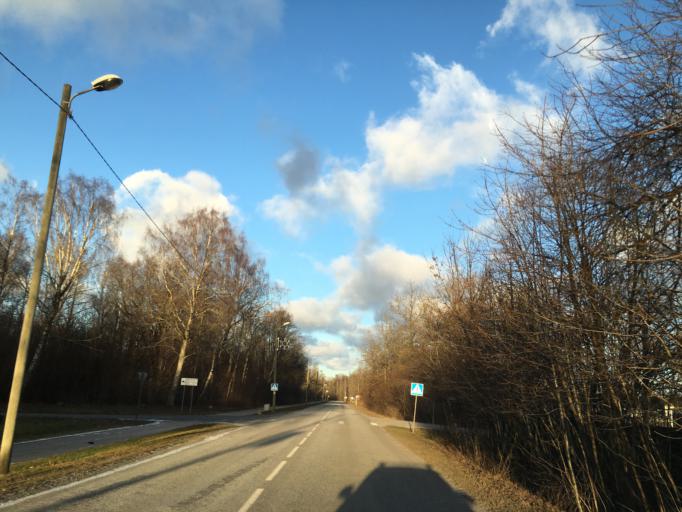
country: EE
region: Harju
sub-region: Saue linn
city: Saue
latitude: 59.3136
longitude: 24.5610
